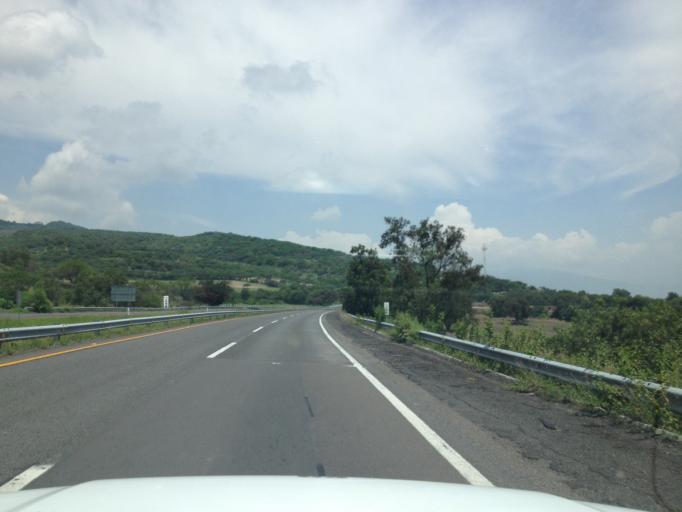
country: MX
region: Michoacan
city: Copandaro de Galeana
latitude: 19.8820
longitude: -101.2186
